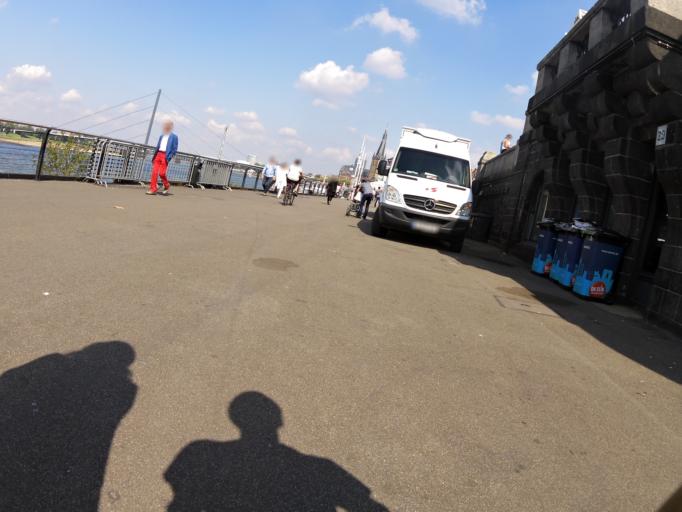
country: DE
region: North Rhine-Westphalia
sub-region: Regierungsbezirk Dusseldorf
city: Dusseldorf
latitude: 51.2243
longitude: 6.7693
